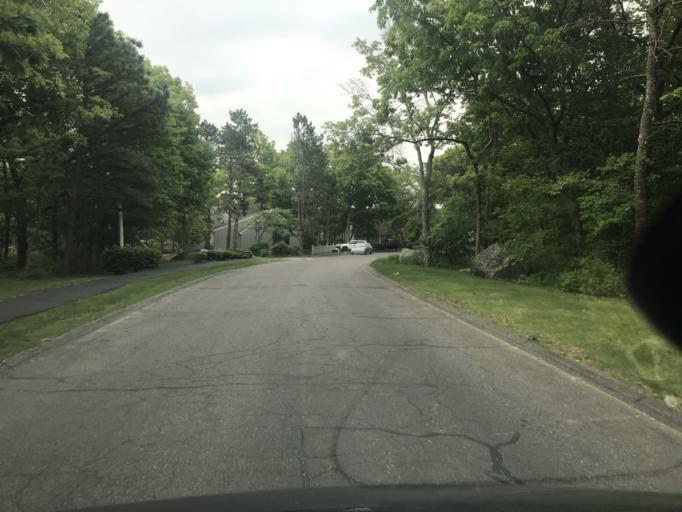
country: US
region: Massachusetts
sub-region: Essex County
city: Rockport
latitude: 42.6649
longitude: -70.6265
